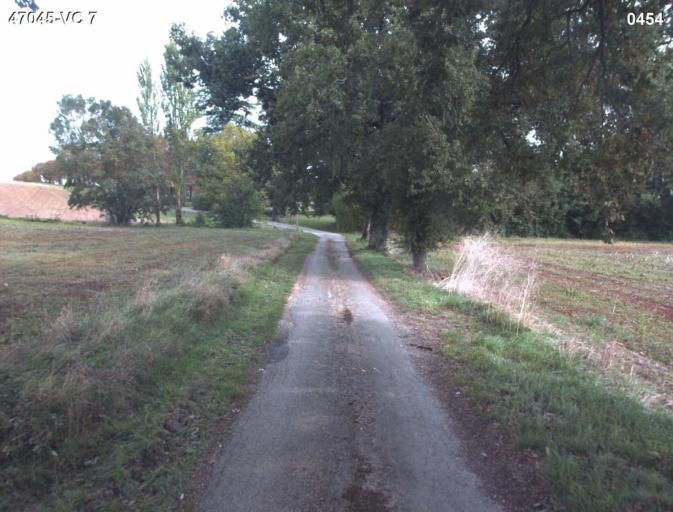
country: FR
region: Aquitaine
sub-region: Departement du Lot-et-Garonne
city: Nerac
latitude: 44.1361
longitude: 0.4321
